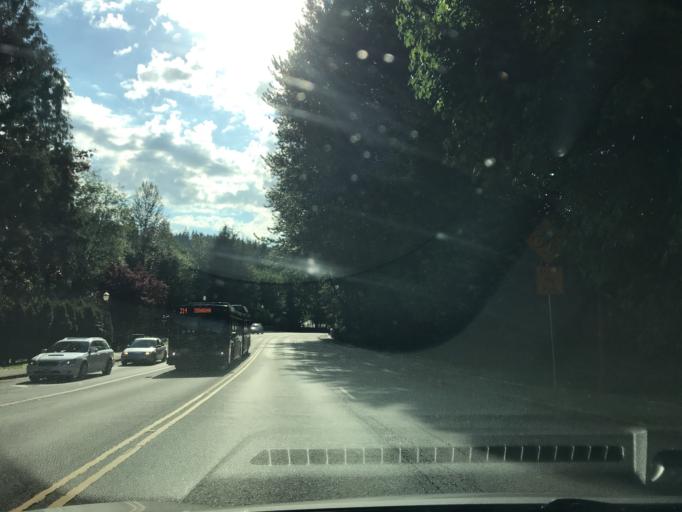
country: US
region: Washington
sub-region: King County
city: Issaquah
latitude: 47.5275
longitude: -122.0368
